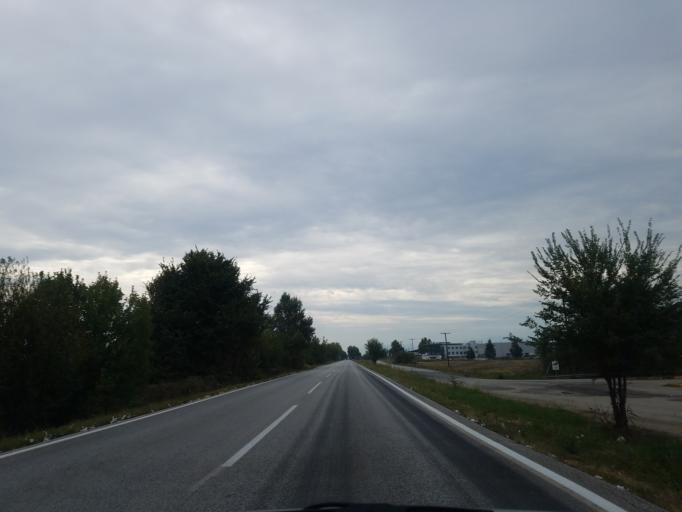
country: GR
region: Thessaly
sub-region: Nomos Kardhitsas
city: Agnantero
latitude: 39.4751
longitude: 21.8467
